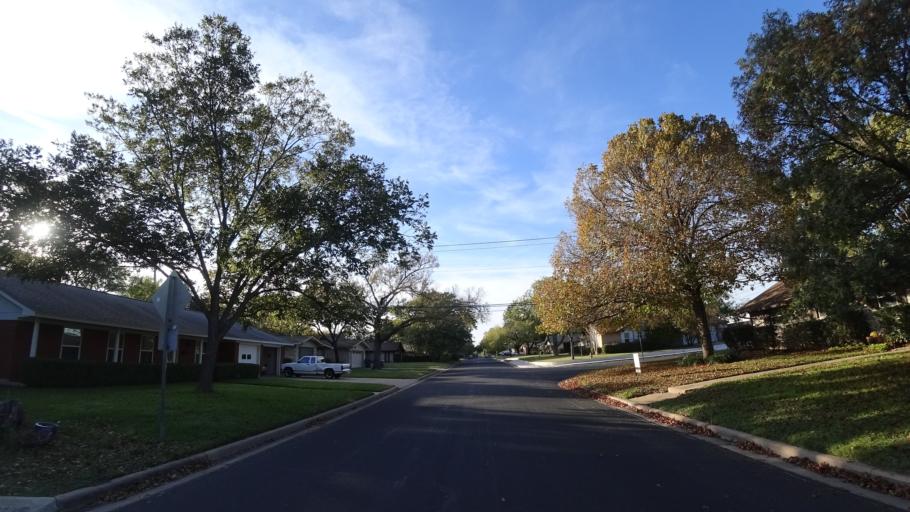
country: US
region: Texas
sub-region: Williamson County
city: Jollyville
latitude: 30.3720
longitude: -97.7298
